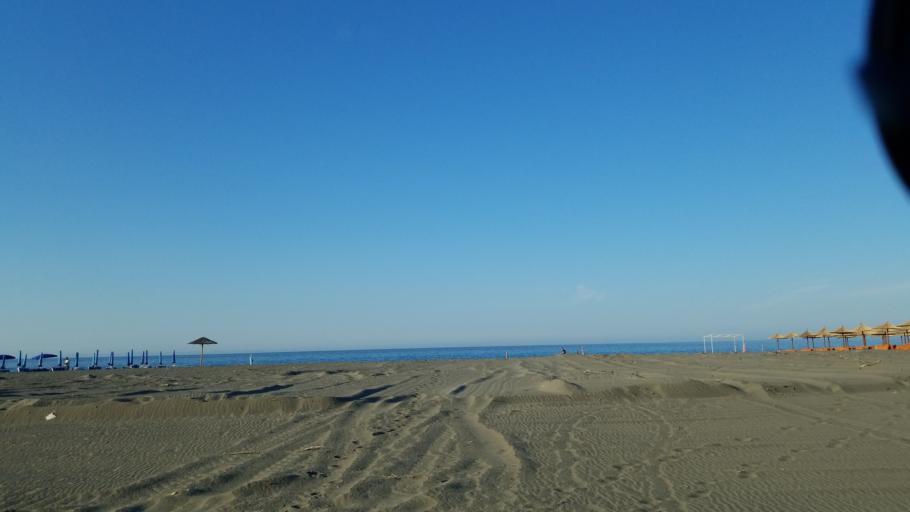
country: AL
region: Shkoder
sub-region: Rrethi i Shkodres
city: Velipoje
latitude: 41.8600
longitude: 19.4388
